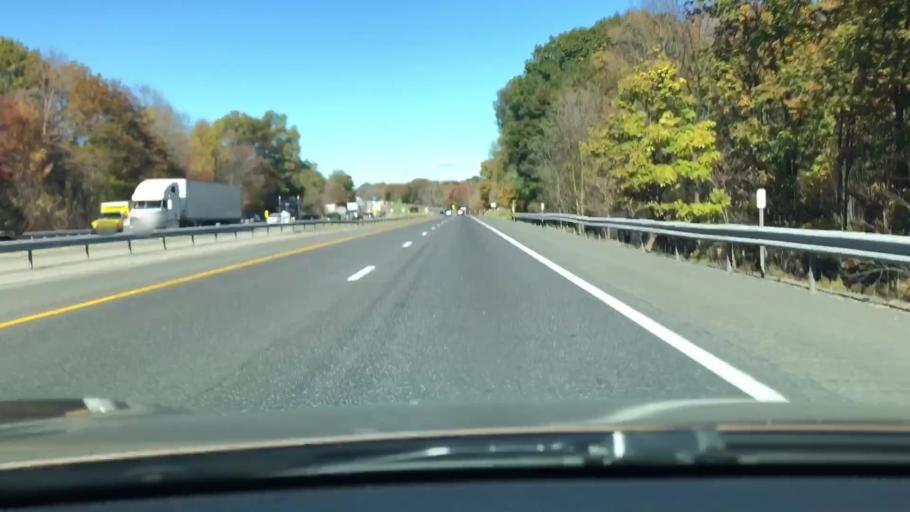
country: US
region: New York
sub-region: Orange County
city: Gardnertown
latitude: 41.5334
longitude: -74.0758
